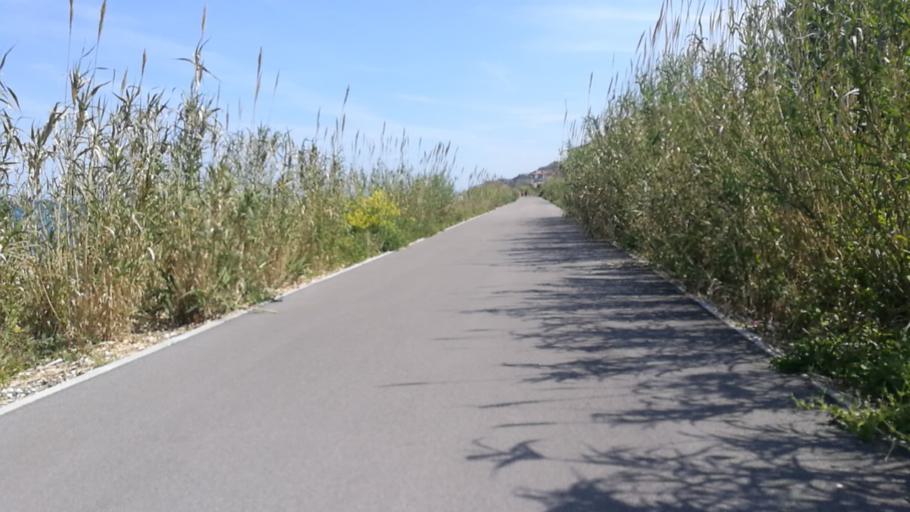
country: IT
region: Abruzzo
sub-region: Provincia di Chieti
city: Marina di San Vito
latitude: 42.3138
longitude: 14.4389
